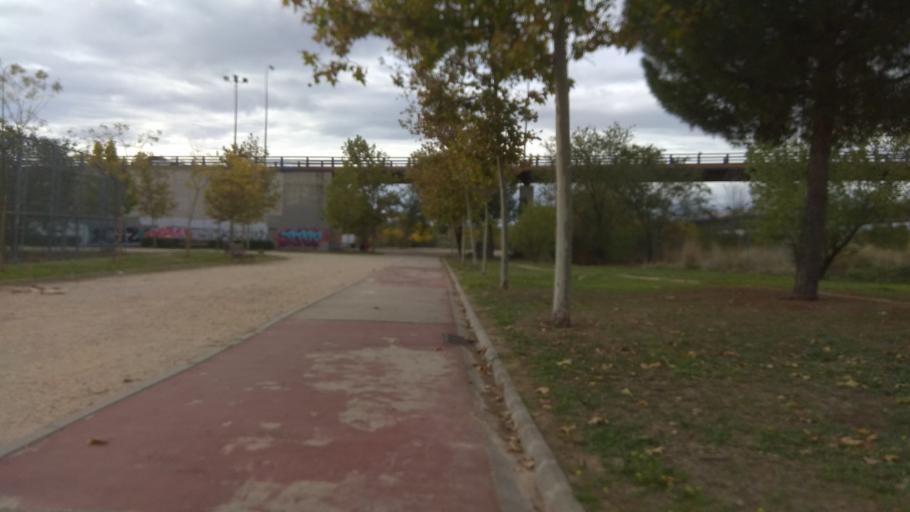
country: ES
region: Madrid
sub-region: Provincia de Madrid
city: Vicalvaro
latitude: 40.4122
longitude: -3.6174
